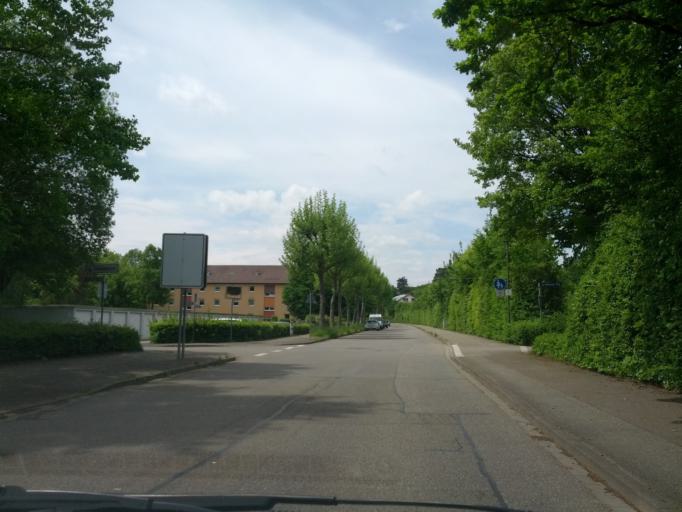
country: DE
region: Baden-Wuerttemberg
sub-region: Freiburg Region
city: Denzlingen
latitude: 48.0737
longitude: 7.8978
